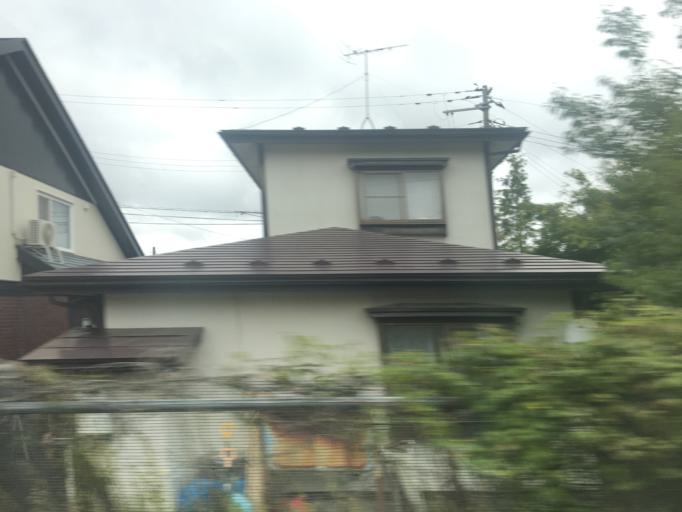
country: JP
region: Iwate
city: Morioka-shi
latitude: 39.7113
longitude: 141.1109
